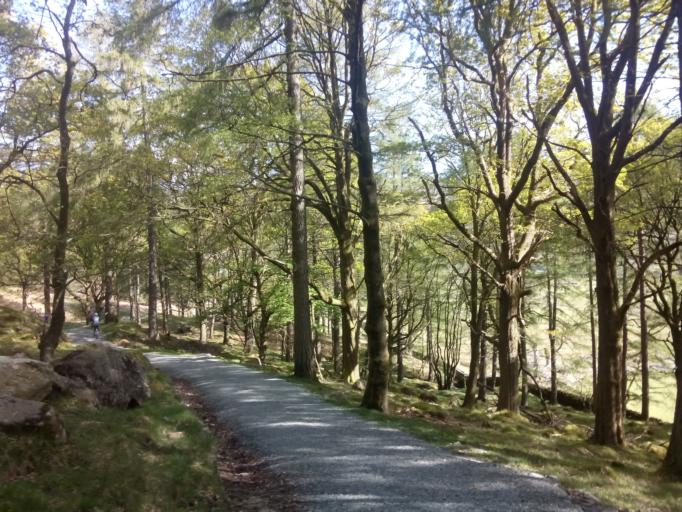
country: GB
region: England
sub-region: Cumbria
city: Ambleside
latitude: 54.4373
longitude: -3.0657
